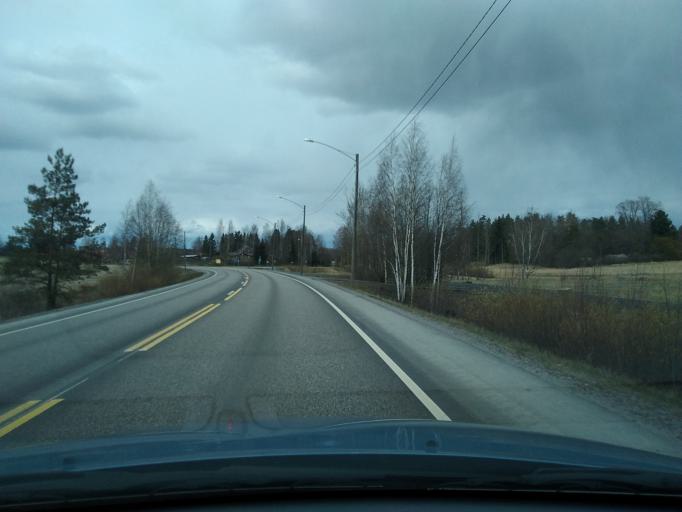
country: FI
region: Uusimaa
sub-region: Helsinki
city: Pornainen
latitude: 60.3355
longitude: 25.4812
